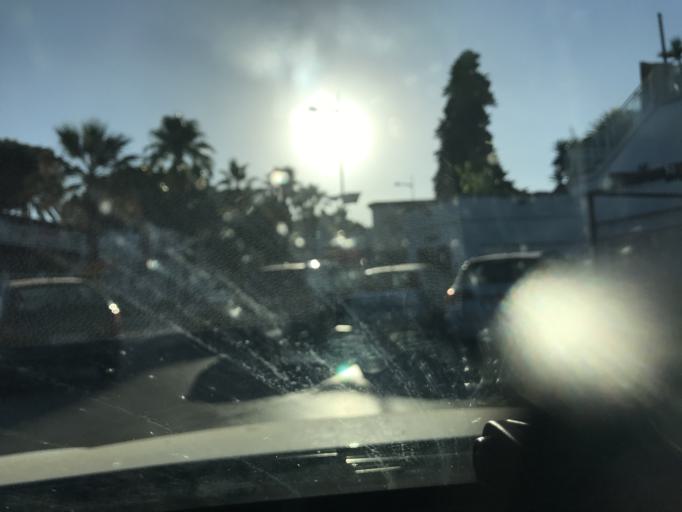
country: ES
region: Andalusia
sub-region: Provincia de Malaga
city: Marbella
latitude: 36.4906
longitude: -4.9575
